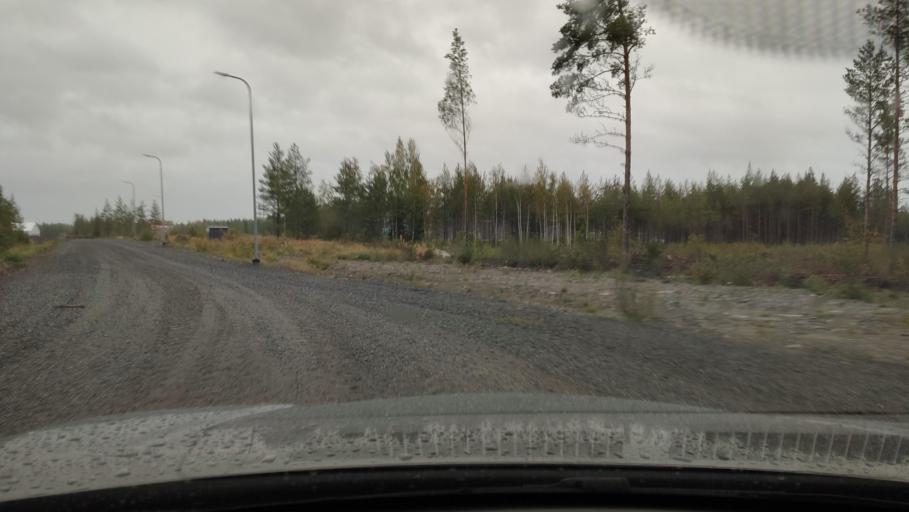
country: FI
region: Ostrobothnia
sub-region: Sydosterbotten
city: Kristinestad
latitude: 62.2278
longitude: 21.5248
